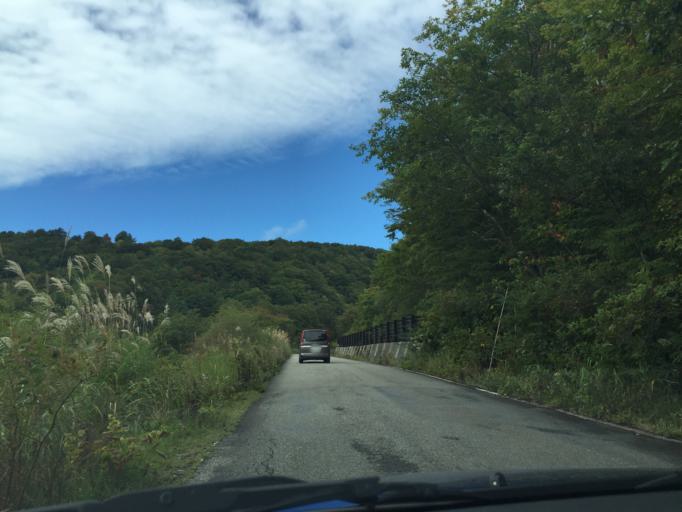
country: JP
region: Fukushima
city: Inawashiro
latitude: 37.6604
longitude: 140.2584
